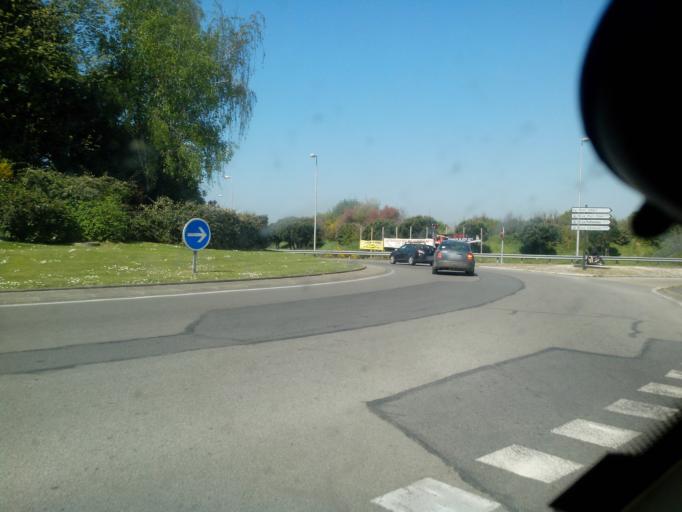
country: FR
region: Pays de la Loire
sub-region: Departement de la Loire-Atlantique
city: Pornic
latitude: 47.1128
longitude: -2.0725
